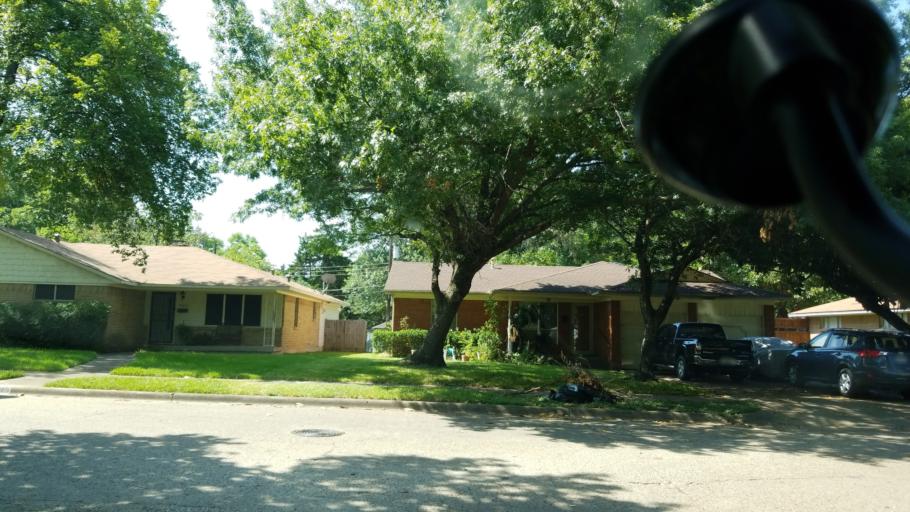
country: US
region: Texas
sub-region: Dallas County
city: Cockrell Hill
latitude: 32.7110
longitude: -96.8774
